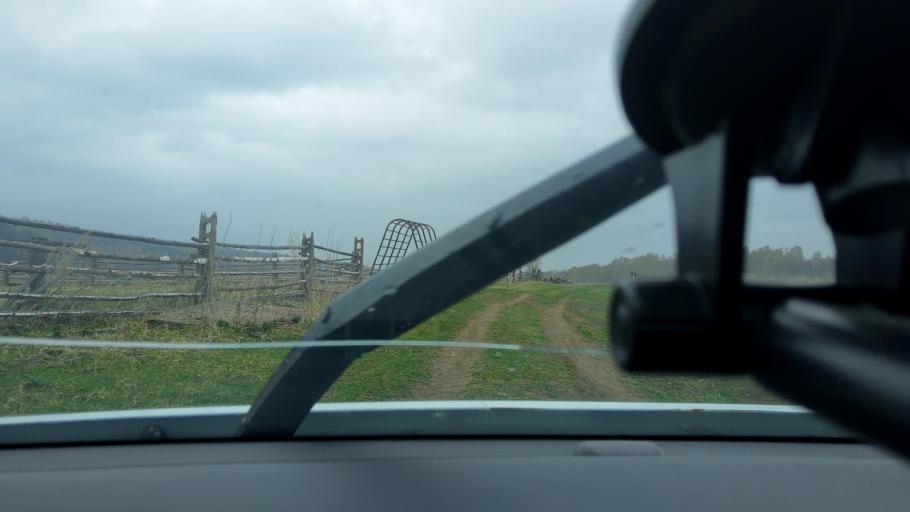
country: RU
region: Bashkortostan
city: Pavlovka
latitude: 55.4345
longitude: 56.3089
